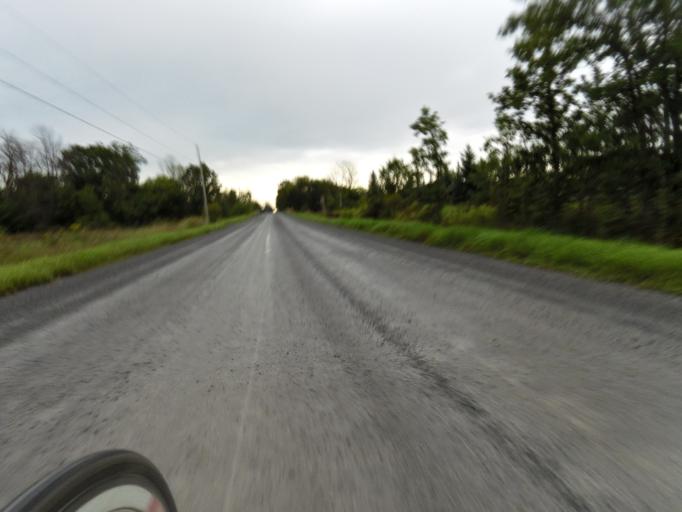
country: CA
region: Ontario
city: Bells Corners
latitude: 45.1865
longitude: -75.7164
